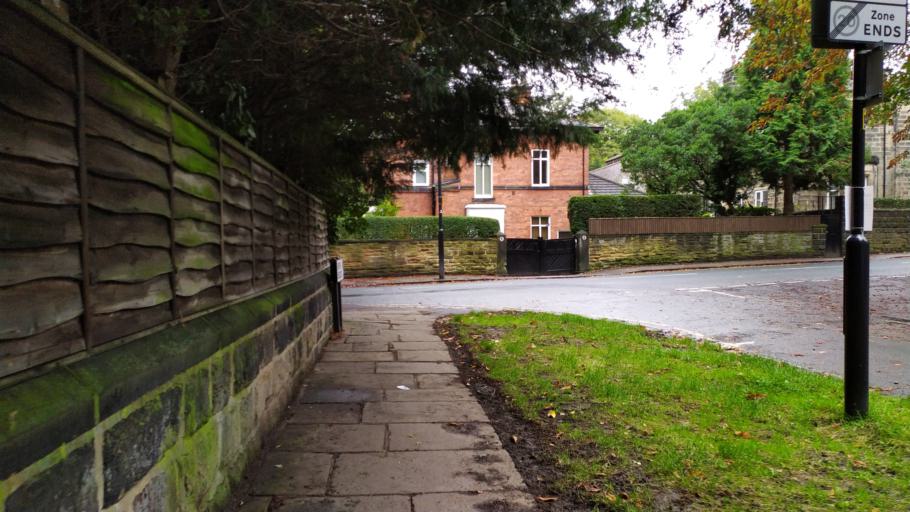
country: GB
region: England
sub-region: City and Borough of Leeds
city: Chapel Allerton
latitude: 53.8249
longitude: -1.5780
